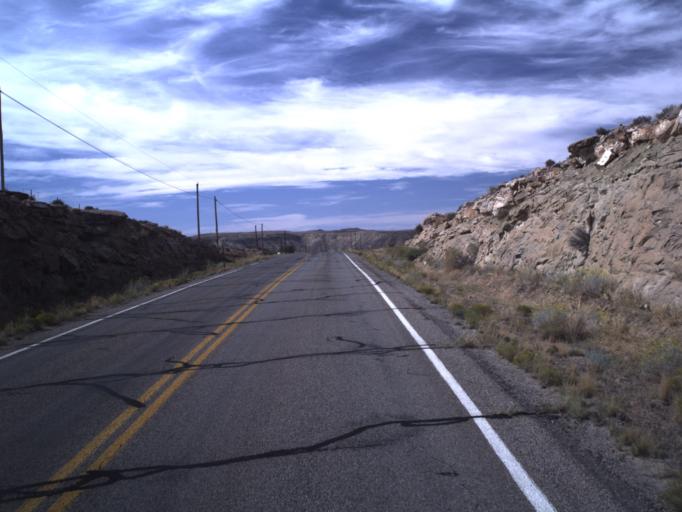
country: US
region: Utah
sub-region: San Juan County
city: Blanding
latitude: 37.2868
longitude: -109.2904
